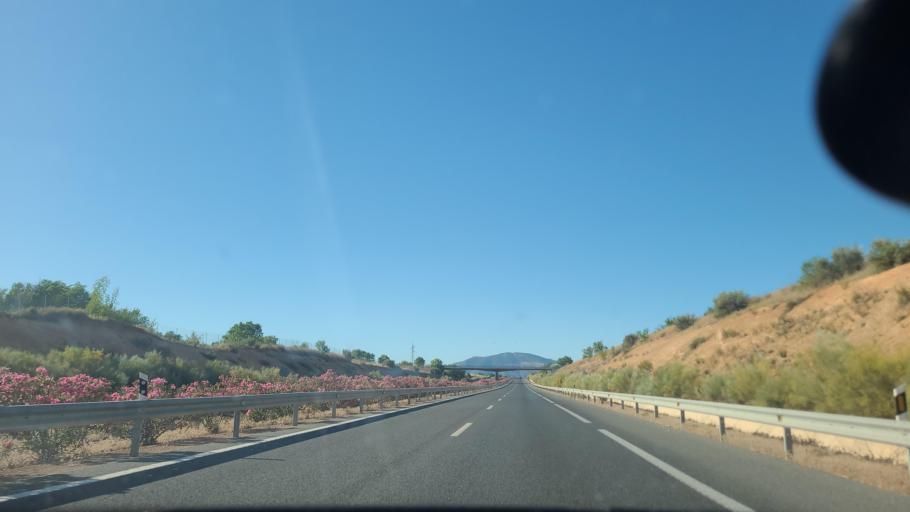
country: ES
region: Andalusia
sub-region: Provincia de Granada
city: Albolote
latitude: 37.2480
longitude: -3.6626
